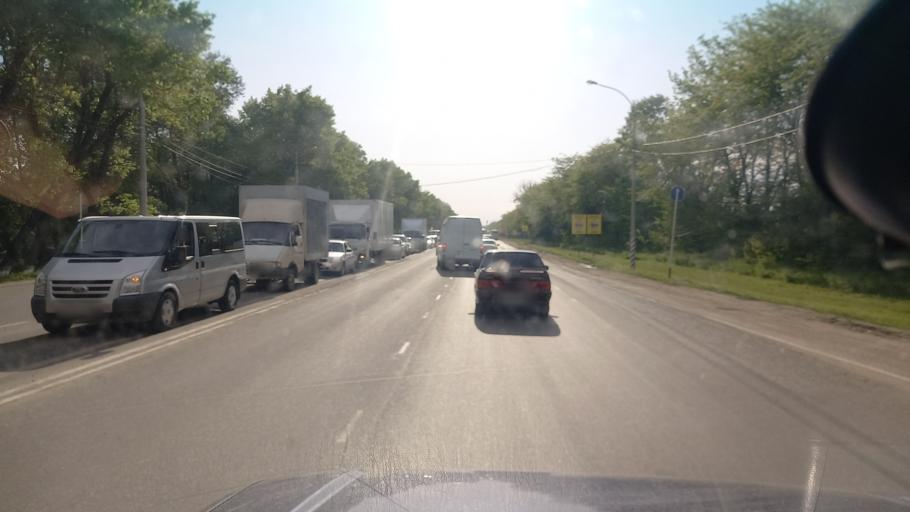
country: RU
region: Adygeya
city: Yablonovskiy
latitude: 45.0565
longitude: 38.8884
